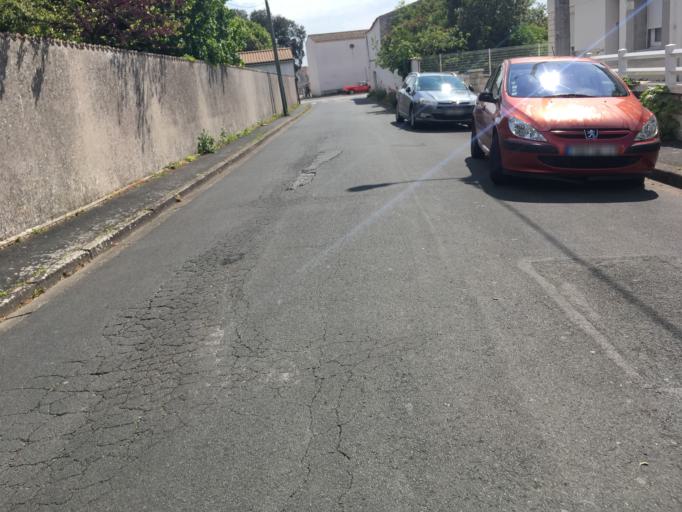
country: FR
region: Poitou-Charentes
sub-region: Departement de la Charente-Maritime
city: Aytre
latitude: 46.1345
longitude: -1.1160
